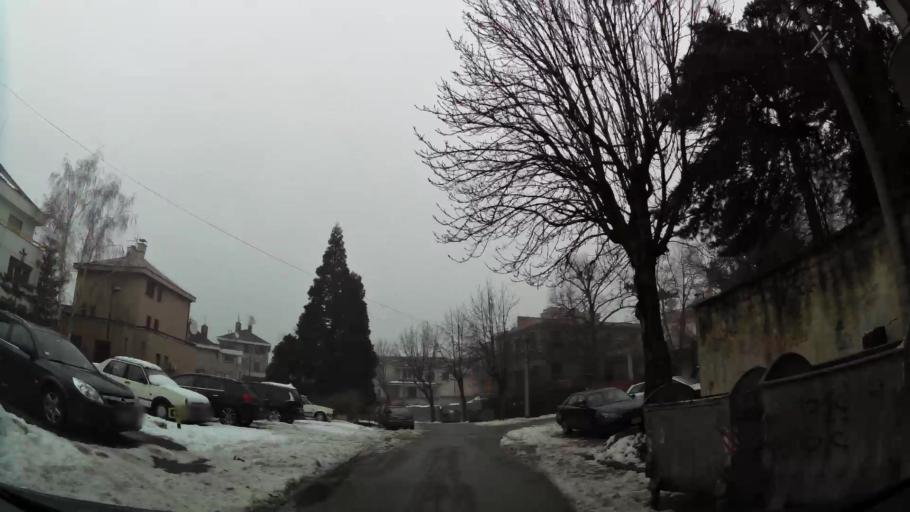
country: RS
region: Central Serbia
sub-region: Belgrade
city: Novi Beograd
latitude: 44.7924
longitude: 20.4336
